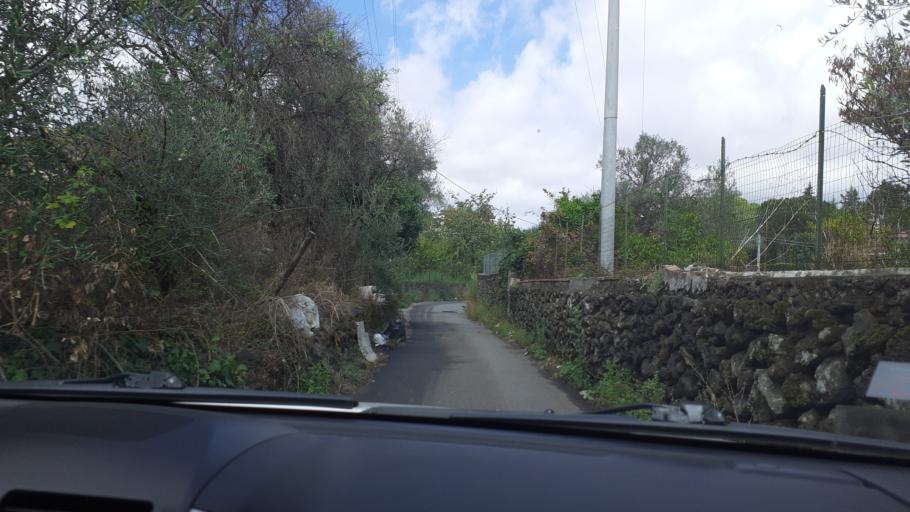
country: IT
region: Sicily
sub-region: Catania
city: Trecastagni
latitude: 37.5972
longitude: 15.0770
